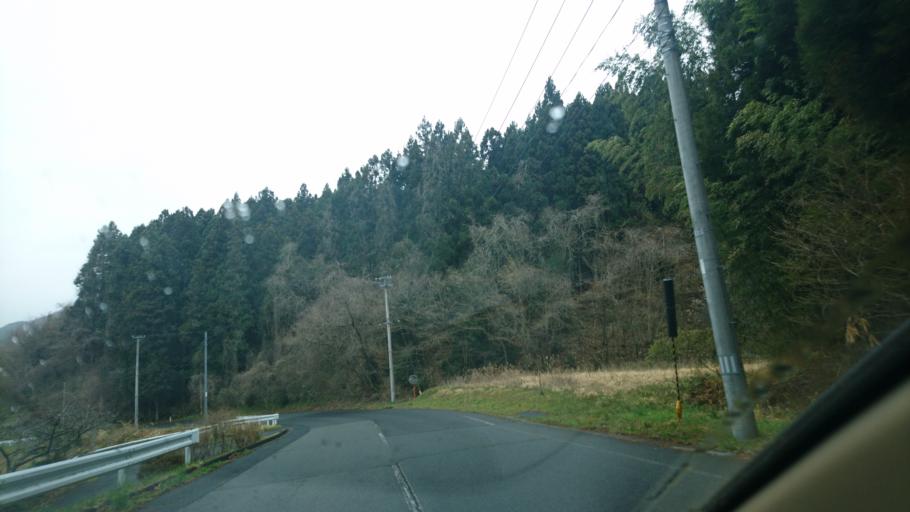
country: JP
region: Iwate
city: Ichinoseki
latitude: 38.9341
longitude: 141.3175
